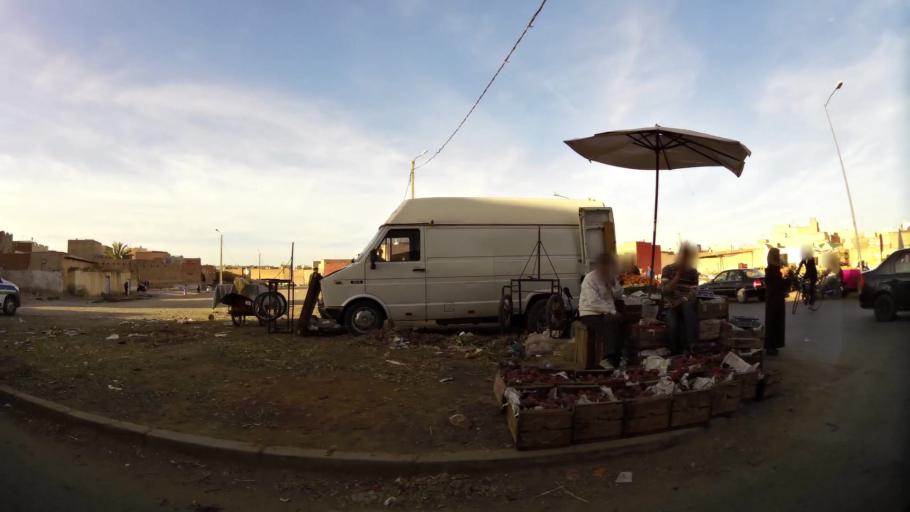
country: MA
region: Oriental
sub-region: Oujda-Angad
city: Oujda
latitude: 34.6768
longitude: -1.9035
